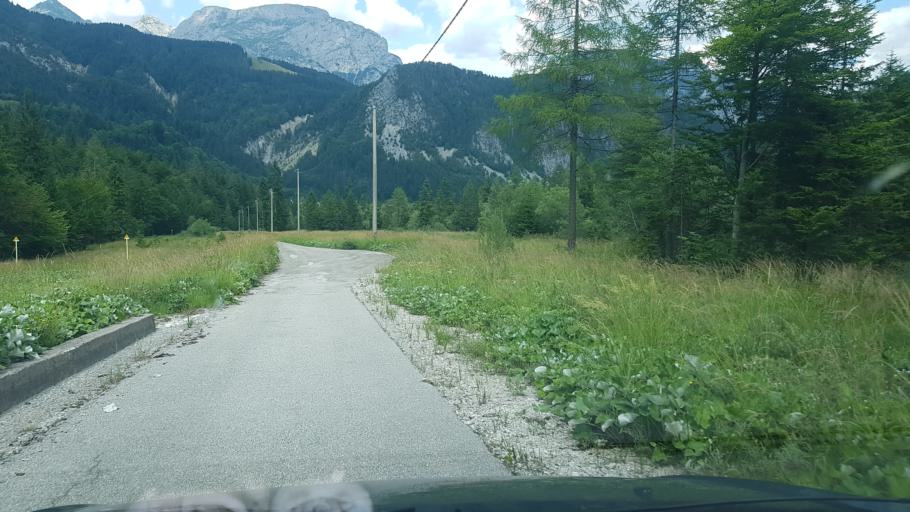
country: IT
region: Friuli Venezia Giulia
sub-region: Provincia di Udine
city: Pontebba
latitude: 46.4947
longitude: 13.2542
